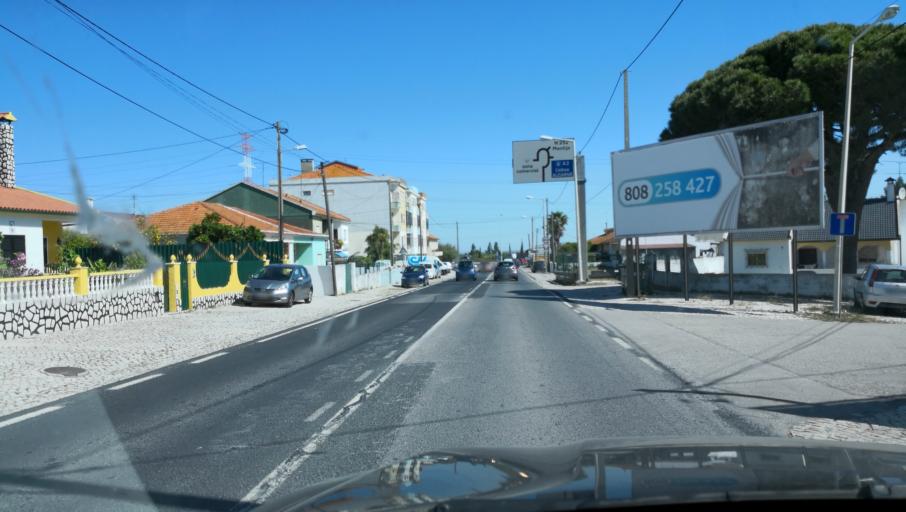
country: PT
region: Setubal
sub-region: Palmela
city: Palmela
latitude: 38.5824
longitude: -8.8902
